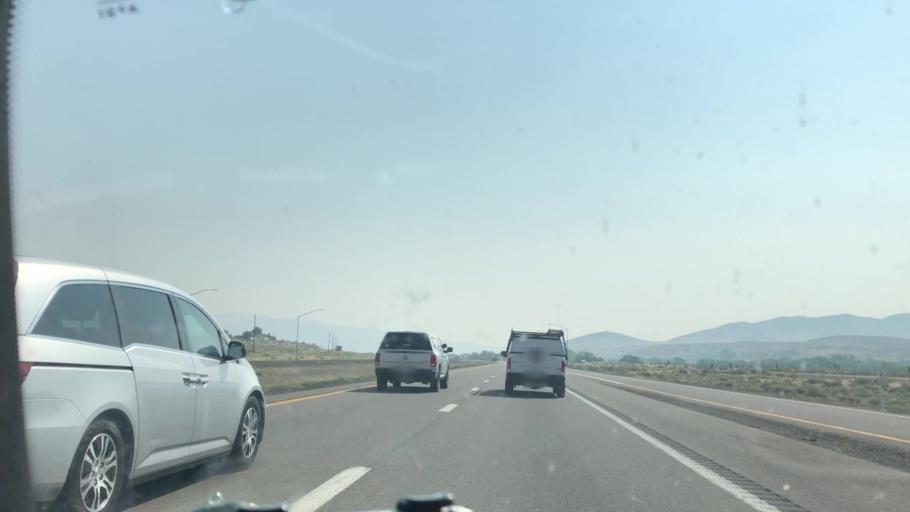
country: US
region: Nevada
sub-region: Lyon County
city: Fernley
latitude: 39.6037
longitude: -119.3319
